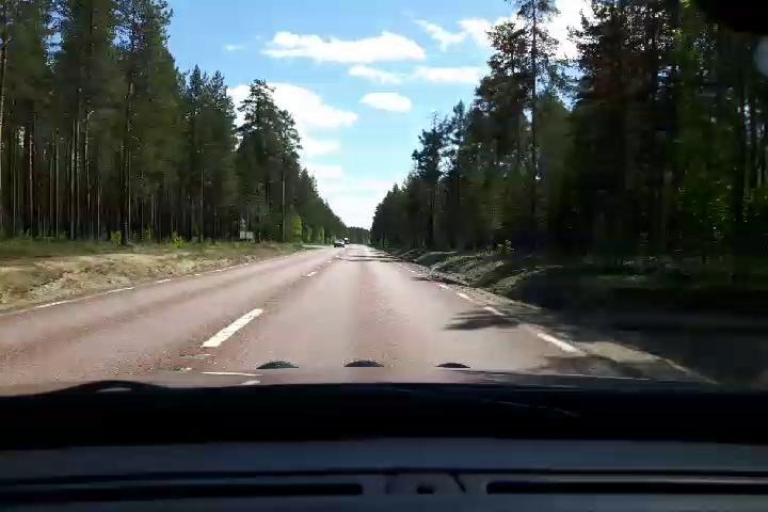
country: SE
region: Gaevleborg
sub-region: Ljusdals Kommun
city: Farila
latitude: 61.8292
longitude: 15.7528
